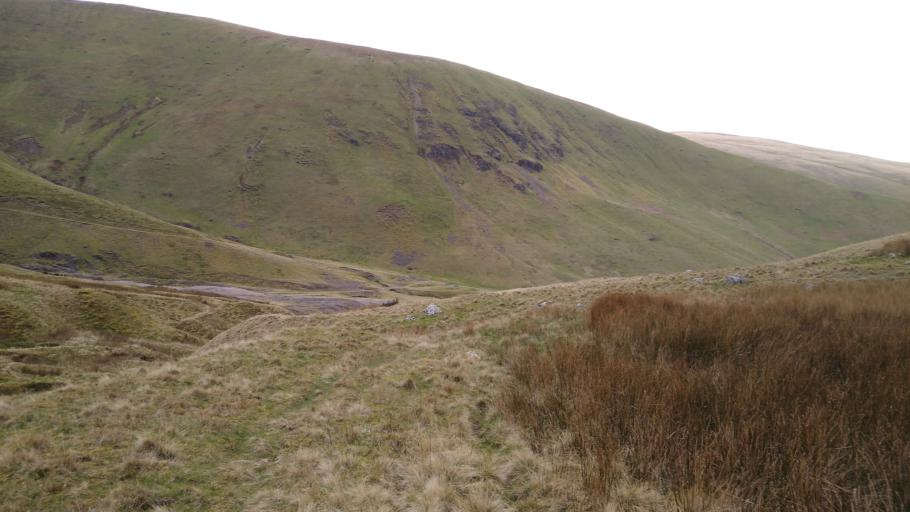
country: GB
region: England
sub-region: Cumbria
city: Keswick
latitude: 54.7013
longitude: -3.0805
